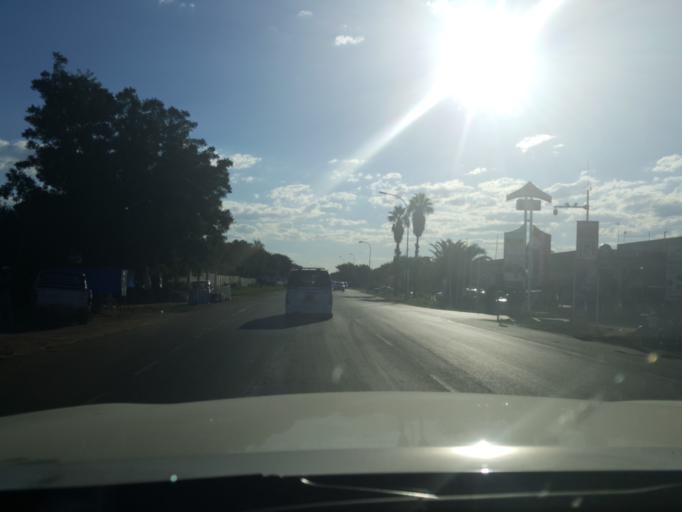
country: BW
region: South East
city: Gaborone
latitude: -24.6446
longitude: 25.9322
